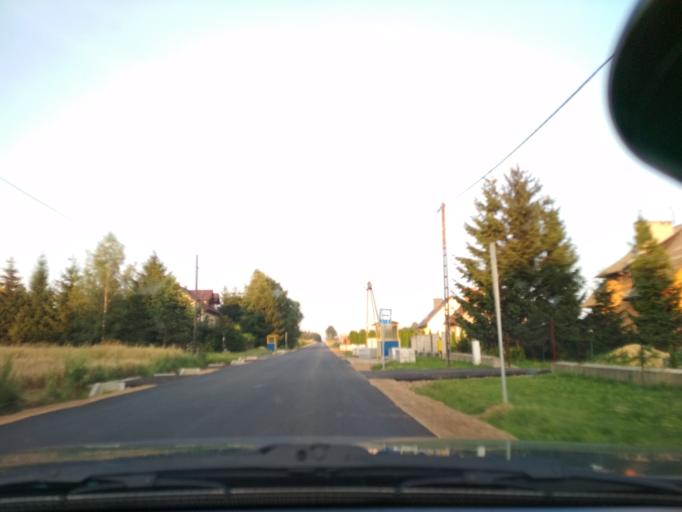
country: PL
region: Lesser Poland Voivodeship
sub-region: Powiat olkuski
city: Wolbrom
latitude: 50.4079
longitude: 19.7901
